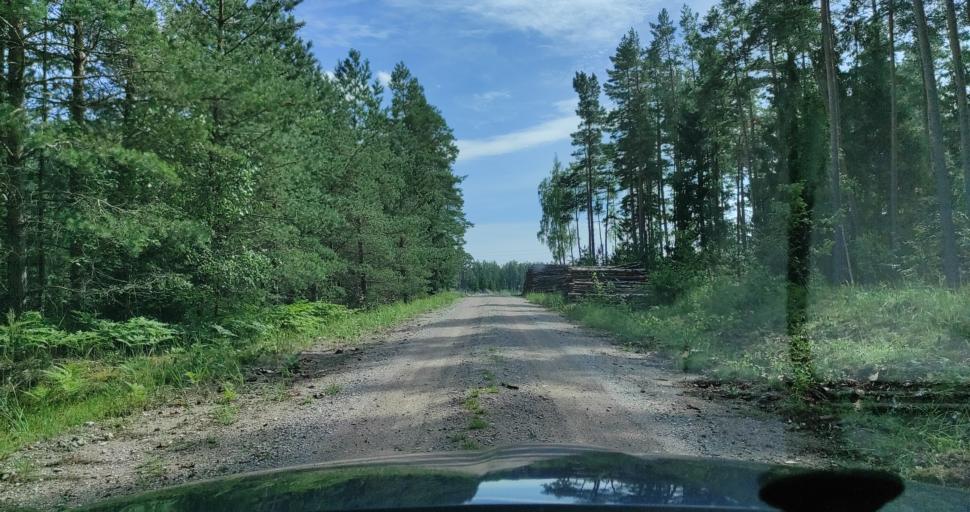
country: LV
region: Pavilostas
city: Pavilosta
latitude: 56.7693
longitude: 21.2936
